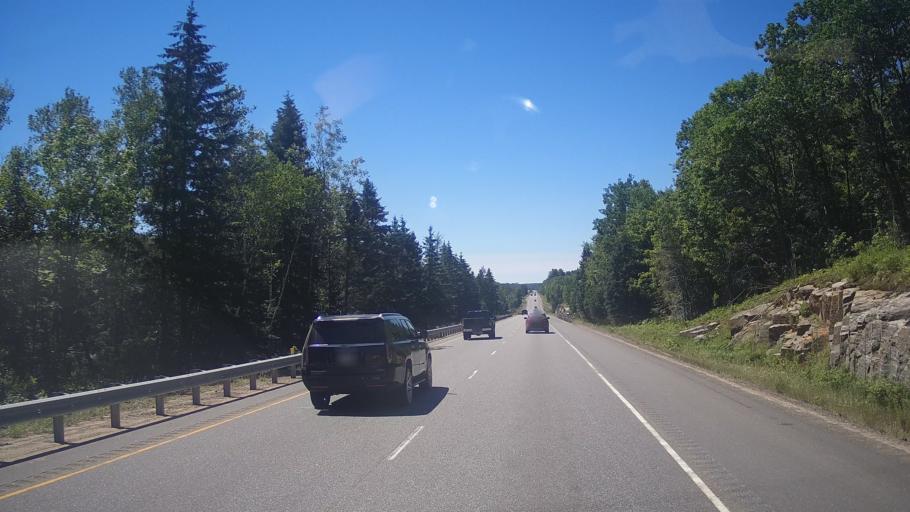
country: CA
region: Ontario
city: Bracebridge
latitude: 45.1458
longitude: -79.3116
